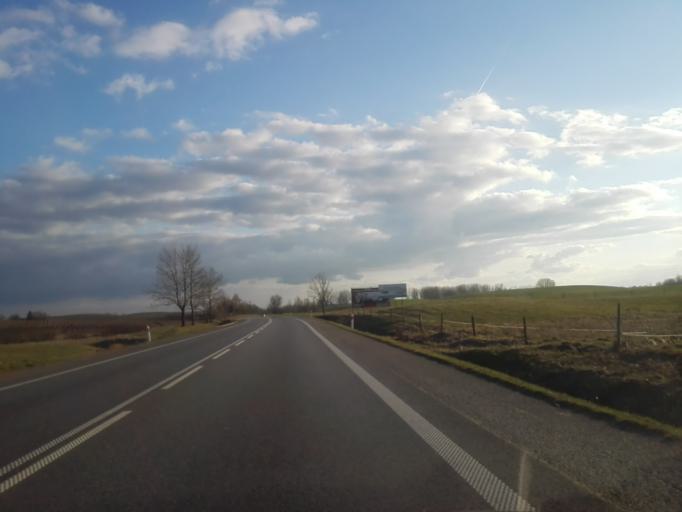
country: PL
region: Podlasie
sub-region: Suwalki
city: Suwalki
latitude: 54.2015
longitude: 23.0213
